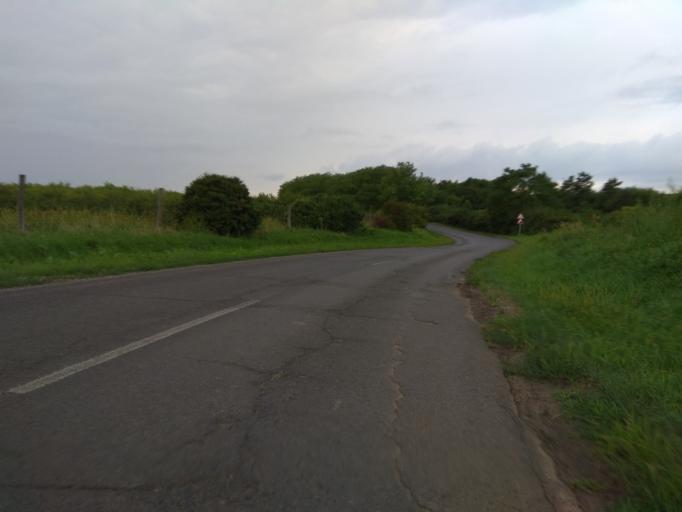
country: HU
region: Borsod-Abauj-Zemplen
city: Monok
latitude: 48.1730
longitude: 21.1172
